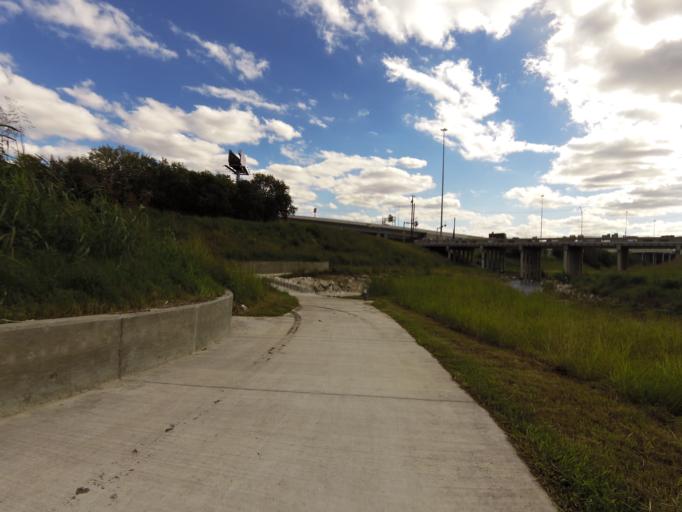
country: US
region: Texas
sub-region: Bexar County
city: San Antonio
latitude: 29.4124
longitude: -98.5092
